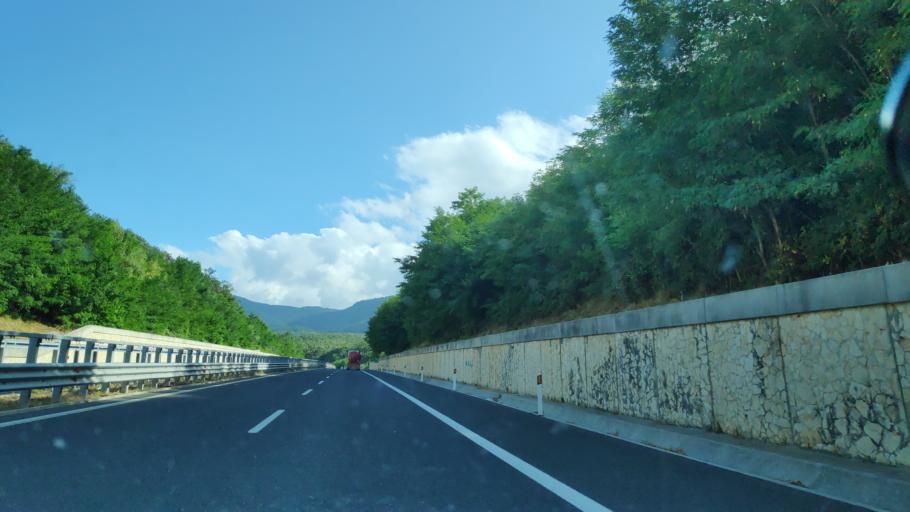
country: IT
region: Campania
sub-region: Provincia di Salerno
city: Casalbuono
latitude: 40.2447
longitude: 15.6597
